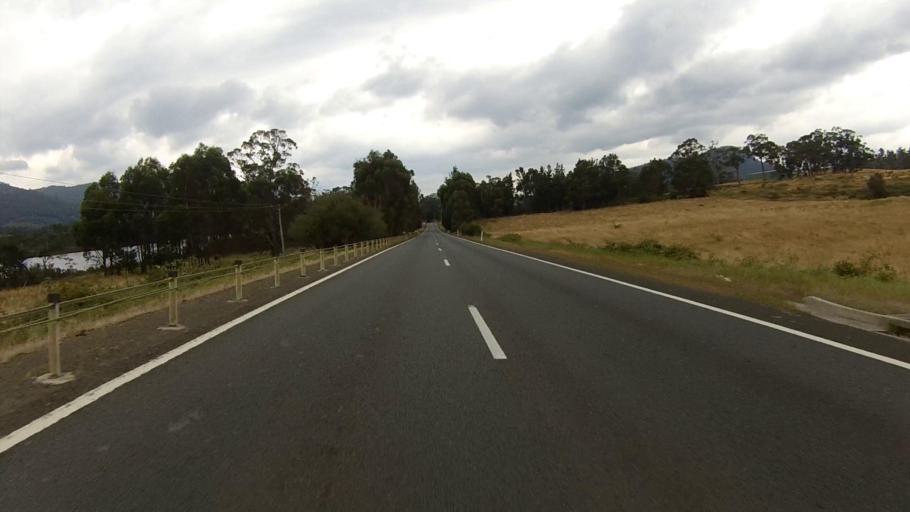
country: AU
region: Tasmania
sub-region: Huon Valley
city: Franklin
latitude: -43.0826
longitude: 147.0308
